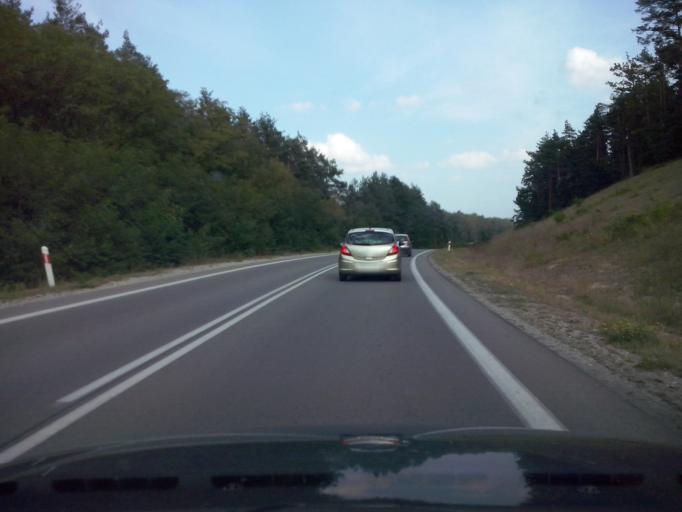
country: PL
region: Subcarpathian Voivodeship
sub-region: Powiat mielecki
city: Przeclaw
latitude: 50.2762
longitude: 21.5352
